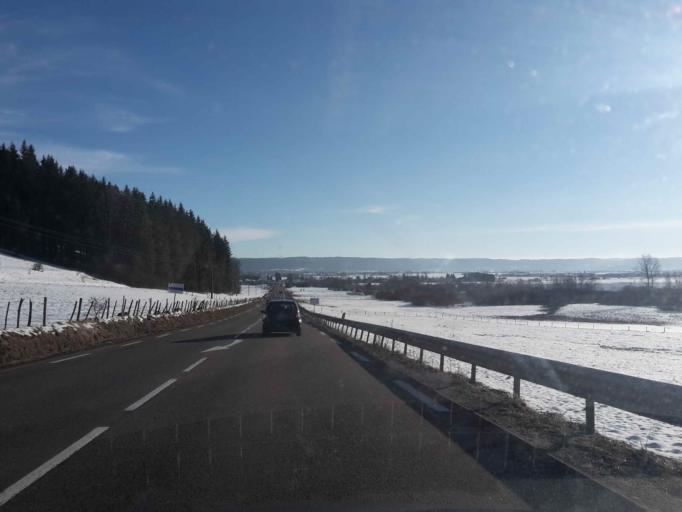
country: FR
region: Franche-Comte
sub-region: Departement du Doubs
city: Doubs
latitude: 46.9555
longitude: 6.3417
